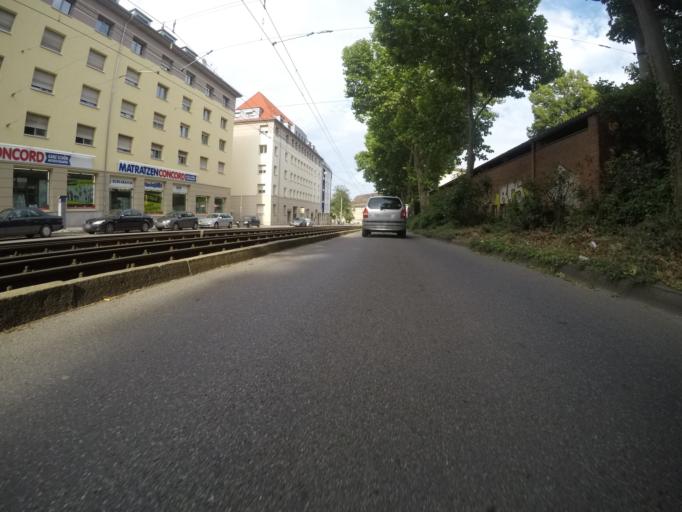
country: DE
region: Baden-Wuerttemberg
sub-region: Regierungsbezirk Stuttgart
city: Stuttgart
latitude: 48.7751
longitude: 9.1570
